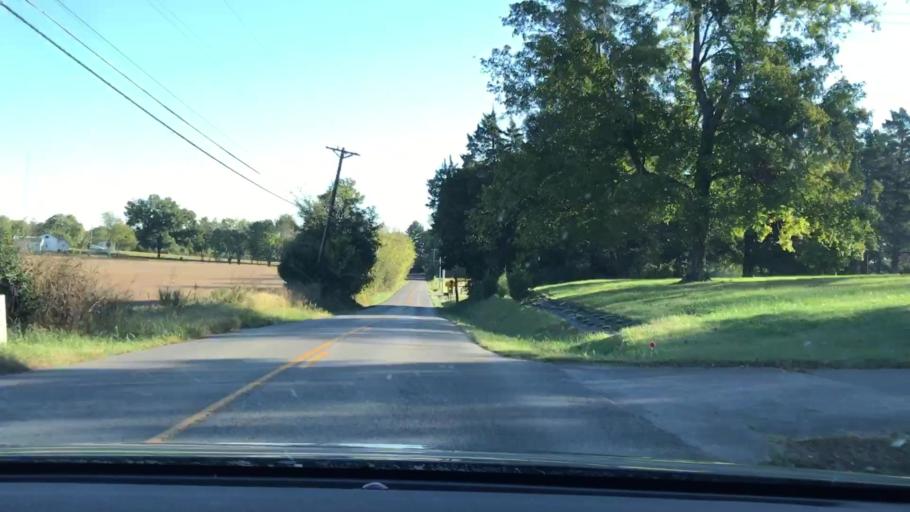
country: US
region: Kentucky
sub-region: Christian County
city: Hopkinsville
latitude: 36.8384
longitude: -87.5242
